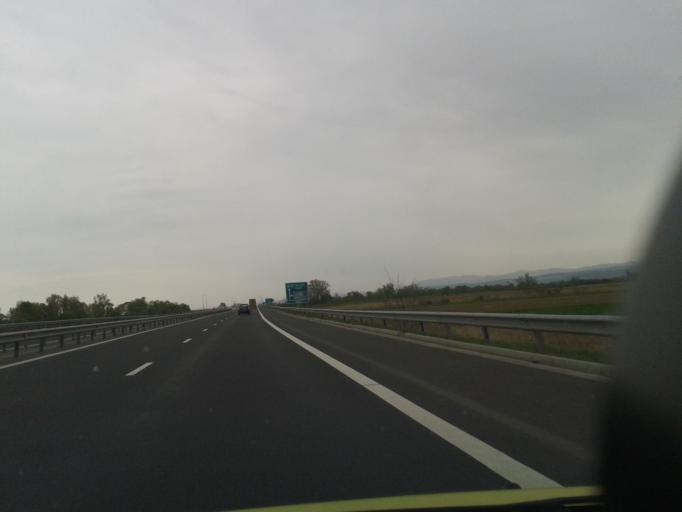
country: RO
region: Hunedoara
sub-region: Comuna Turdas
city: Pricaz
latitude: 45.8750
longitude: 23.1760
